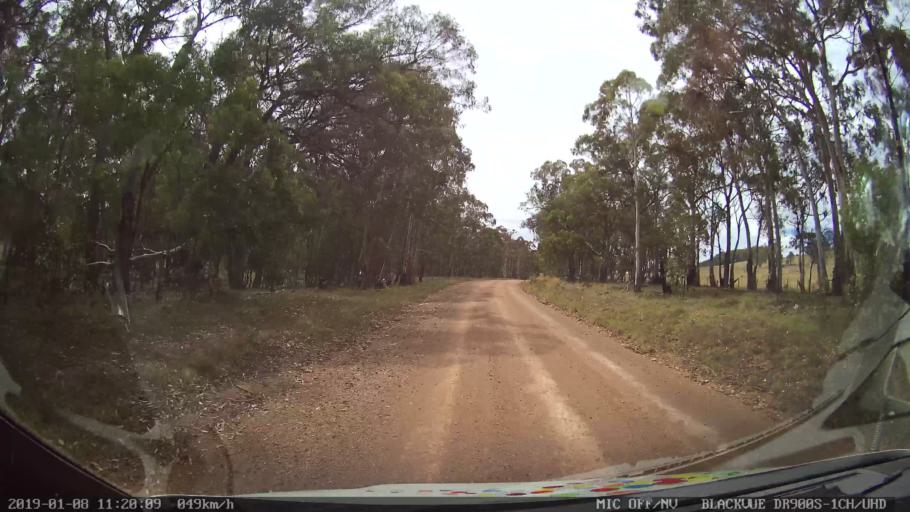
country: AU
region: New South Wales
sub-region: Guyra
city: Guyra
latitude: -30.2293
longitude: 151.5593
